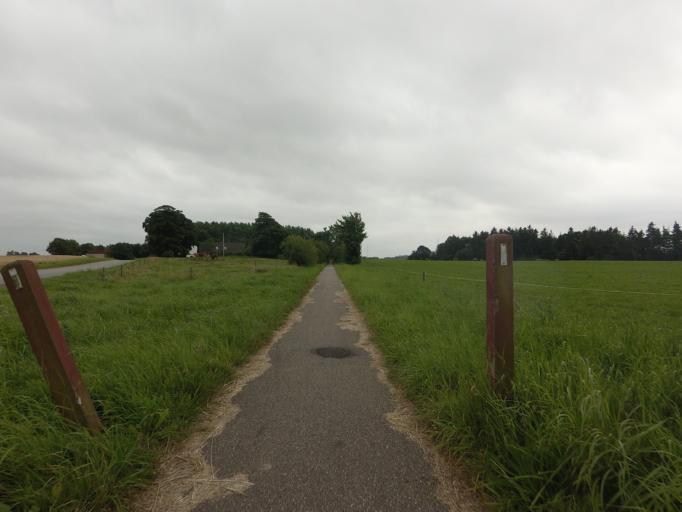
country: DK
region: Central Jutland
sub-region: Horsens Kommune
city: Braedstrup
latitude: 56.0091
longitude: 9.5861
